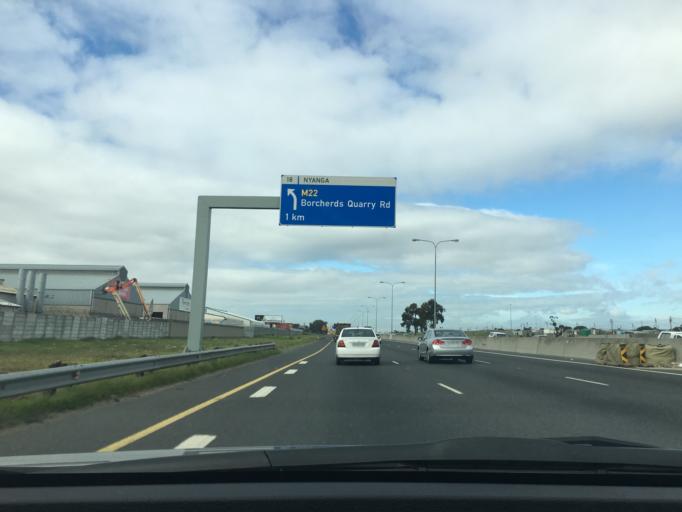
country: ZA
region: Western Cape
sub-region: City of Cape Town
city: Lansdowne
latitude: -33.9709
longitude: 18.5767
